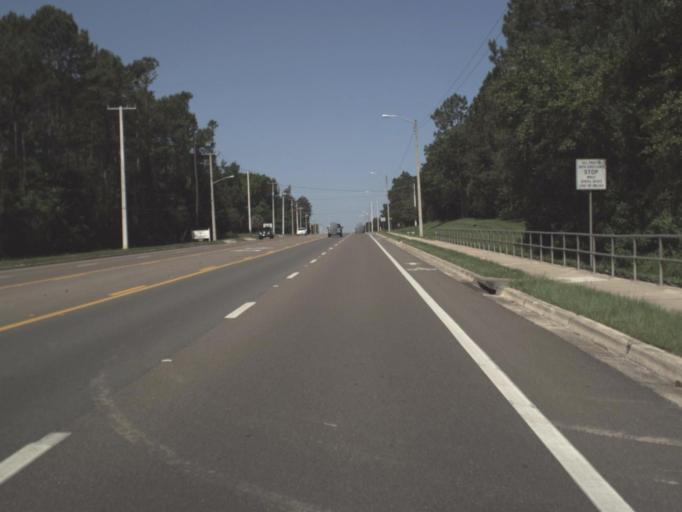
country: US
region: Florida
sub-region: Baker County
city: Macclenny
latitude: 30.2788
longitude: -82.1478
